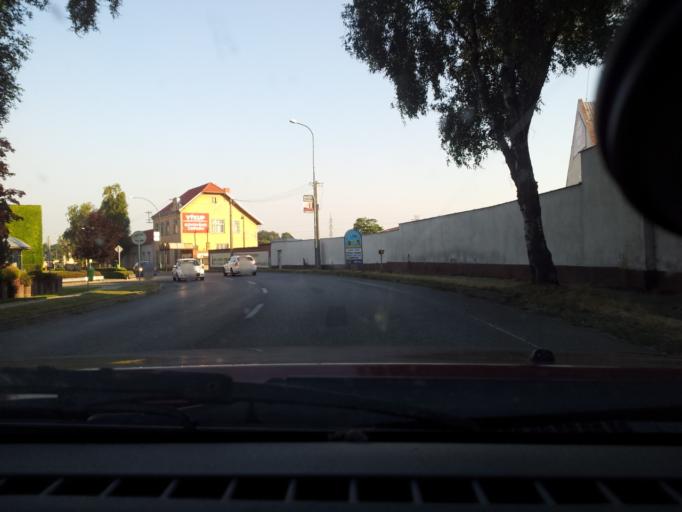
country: CZ
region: South Moravian
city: Hodonin
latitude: 48.8437
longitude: 17.1258
